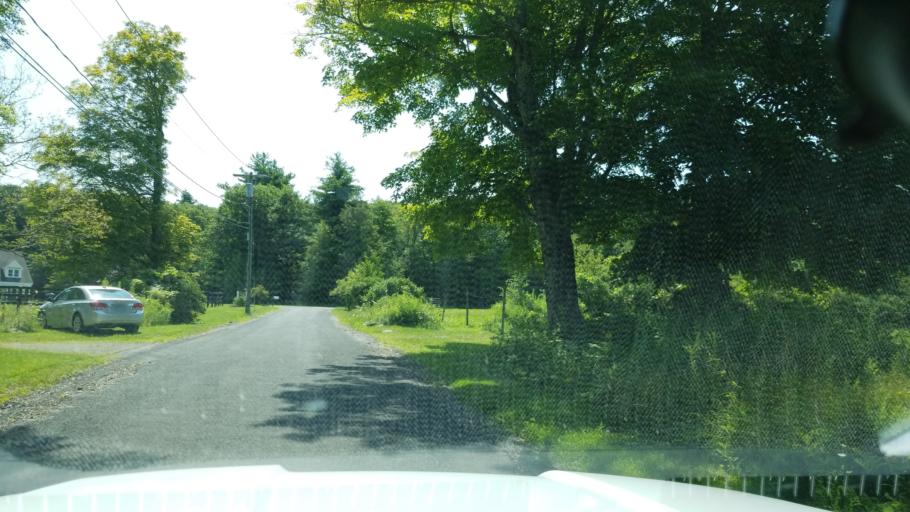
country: US
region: Connecticut
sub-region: Litchfield County
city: Winsted
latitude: 42.0104
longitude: -73.0693
